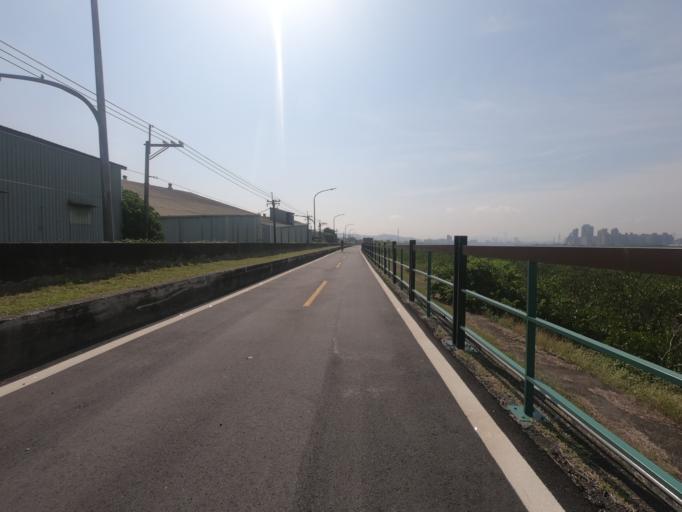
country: TW
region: Taipei
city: Taipei
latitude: 25.1043
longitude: 121.4792
